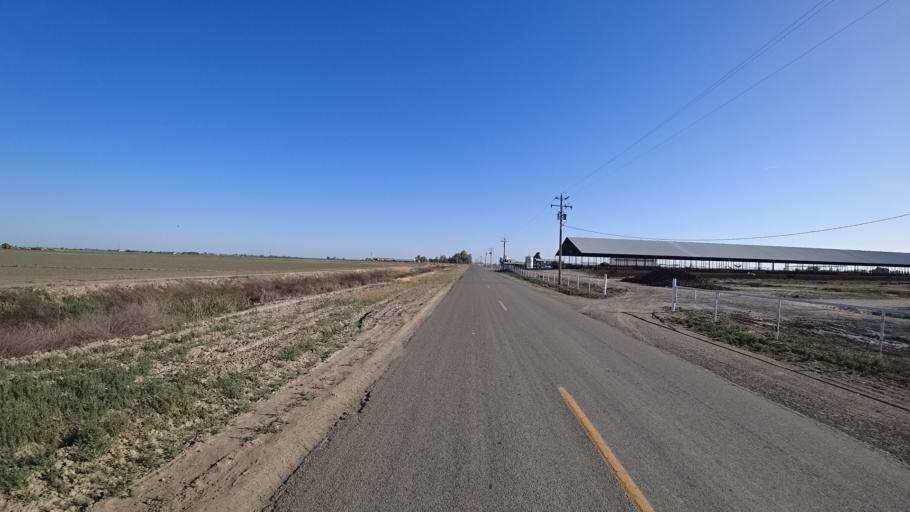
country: US
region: California
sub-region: Kings County
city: Stratford
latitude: 36.1641
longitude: -119.7981
